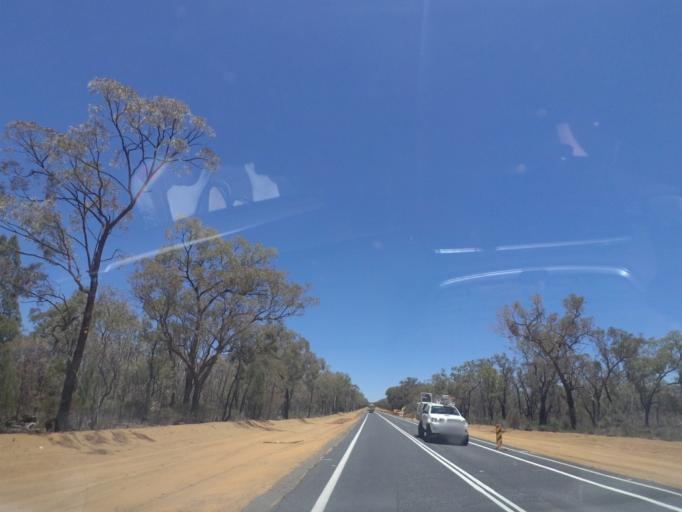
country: AU
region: New South Wales
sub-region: Warrumbungle Shire
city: Coonabarabran
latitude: -30.9281
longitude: 149.4300
